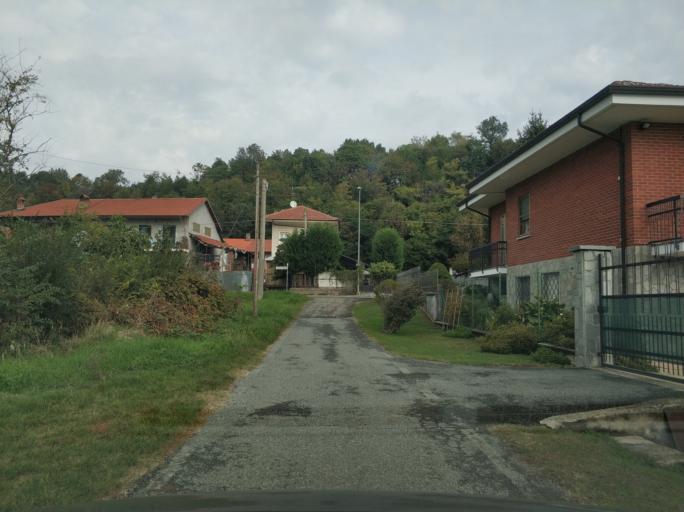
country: IT
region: Piedmont
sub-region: Provincia di Torino
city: Nole
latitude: 45.2566
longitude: 7.5733
